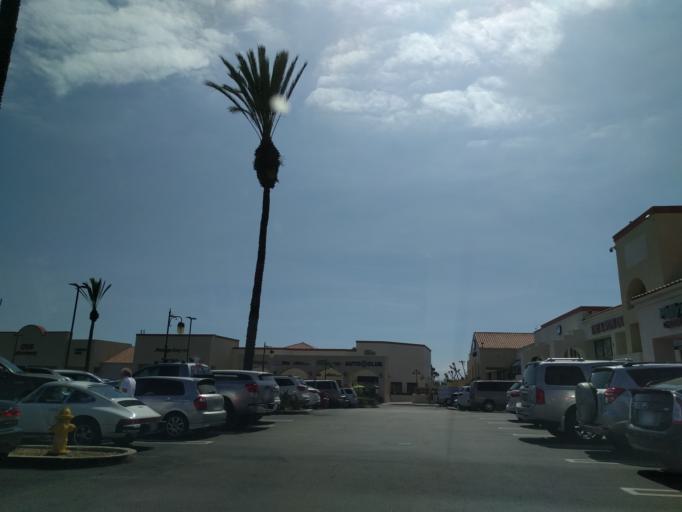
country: US
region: California
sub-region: Orange County
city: San Juan Capistrano
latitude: 33.4589
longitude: -117.6526
